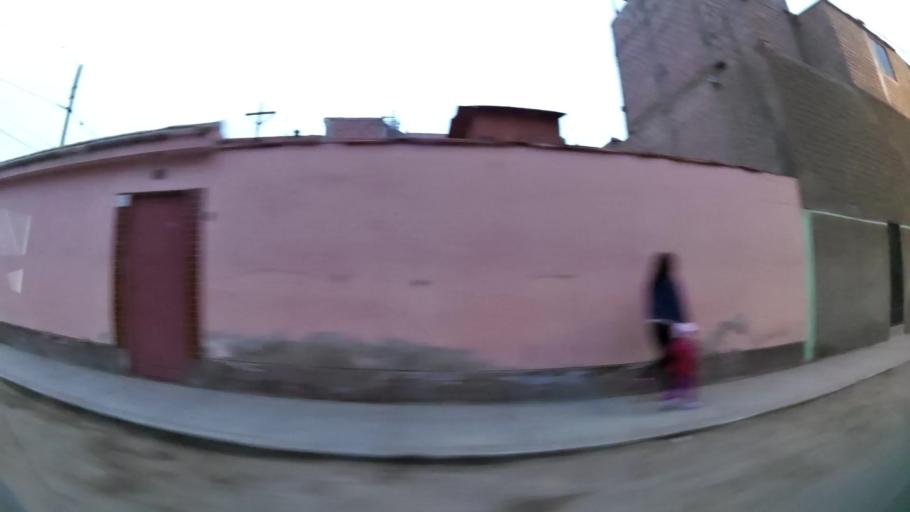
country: PE
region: Callao
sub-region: Callao
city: Callao
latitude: -12.0751
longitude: -77.1123
